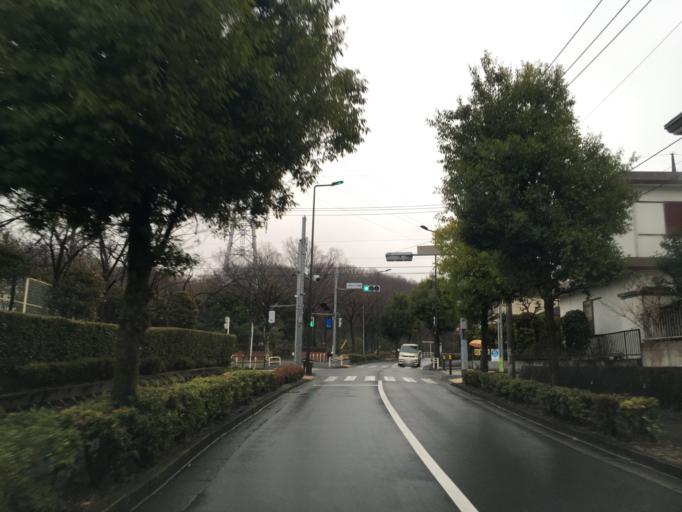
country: JP
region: Tokyo
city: Kokubunji
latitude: 35.6364
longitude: 139.4579
